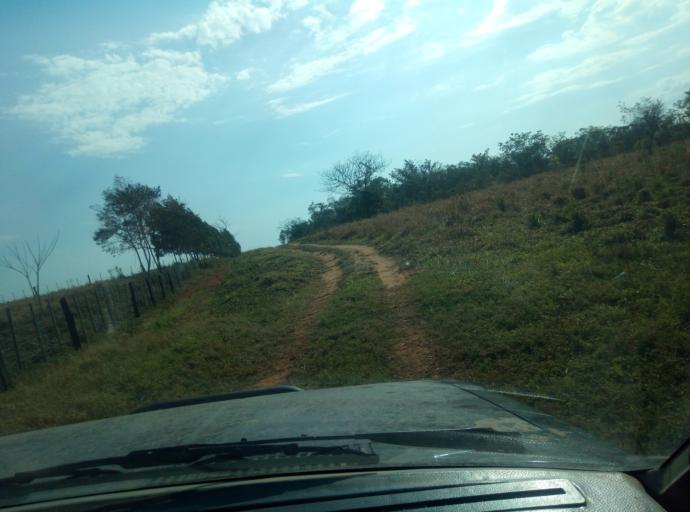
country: PY
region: Caaguazu
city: Doctor Cecilio Baez
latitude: -25.1415
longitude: -56.2590
